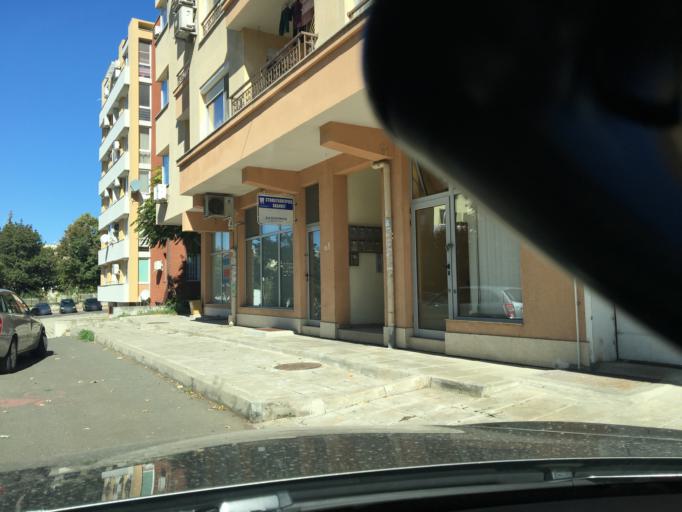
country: BG
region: Burgas
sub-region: Obshtina Burgas
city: Burgas
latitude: 42.5147
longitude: 27.4587
